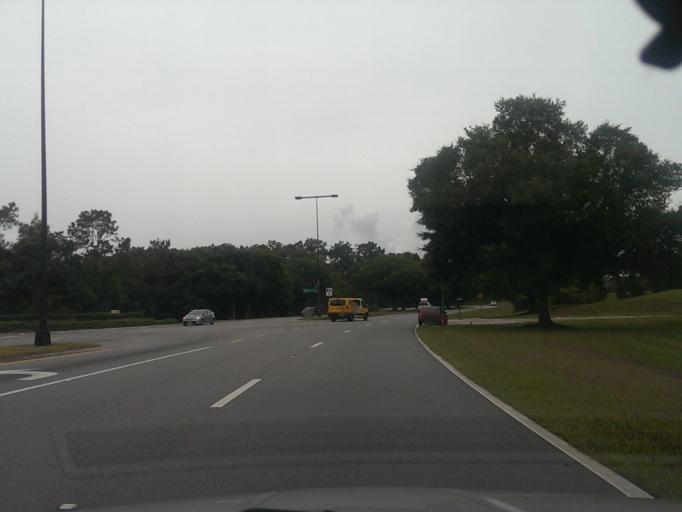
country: US
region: Florida
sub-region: Osceola County
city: Celebration
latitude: 28.3819
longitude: -81.5219
